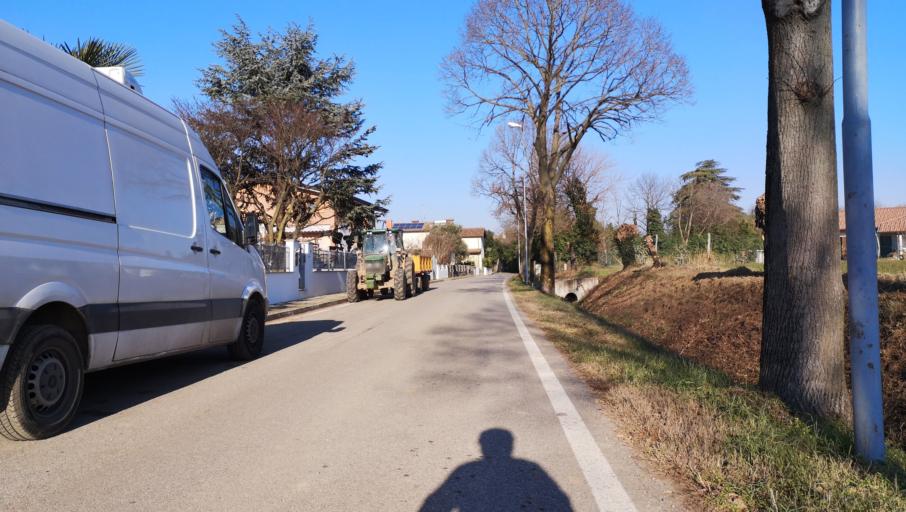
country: IT
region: Friuli Venezia Giulia
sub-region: Provincia di Udine
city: Santa Maria la Longa
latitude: 45.9200
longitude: 13.2971
